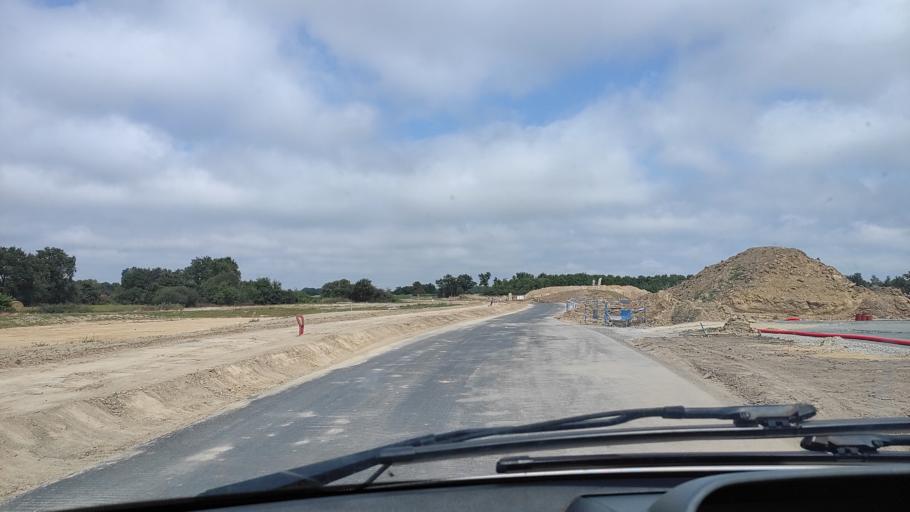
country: FR
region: Pays de la Loire
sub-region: Departement de la Vendee
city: Dompierre-sur-Yon
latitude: 46.7418
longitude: -1.4186
